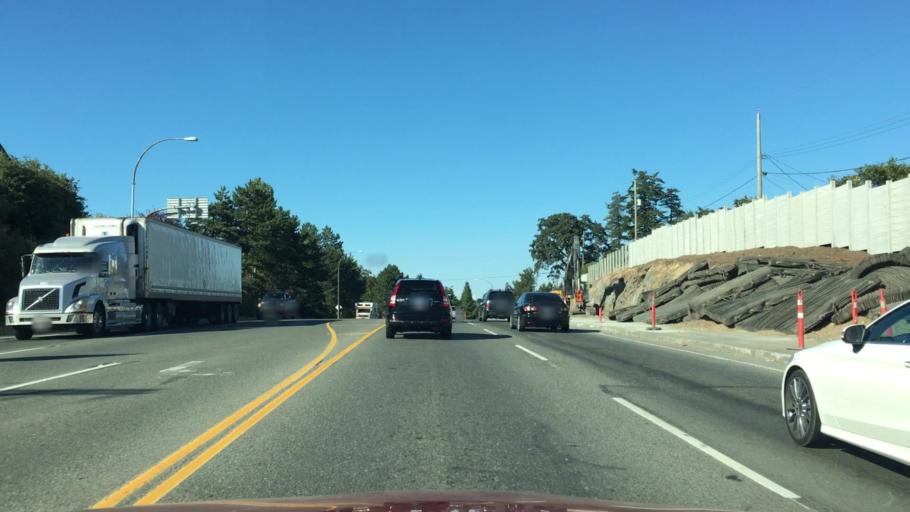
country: CA
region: British Columbia
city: Victoria
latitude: 48.4622
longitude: -123.4020
